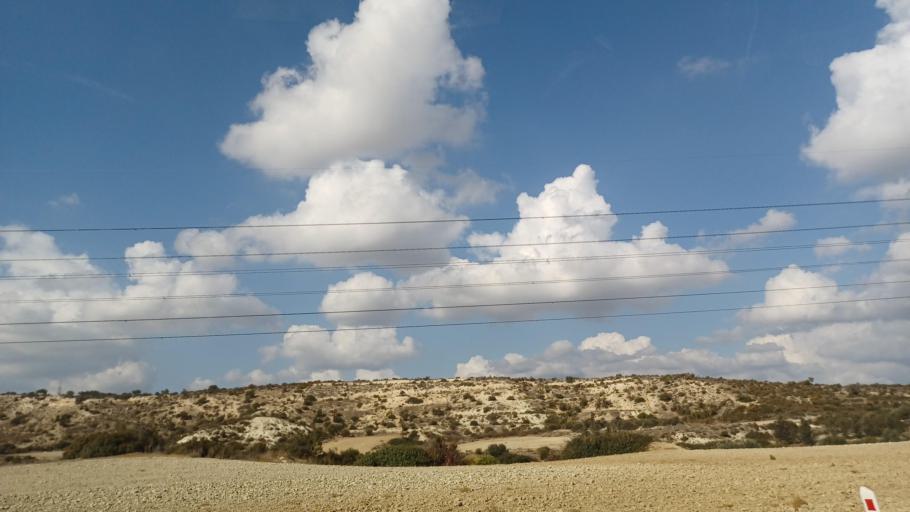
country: CY
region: Limassol
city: Pyrgos
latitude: 34.7436
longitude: 33.2918
